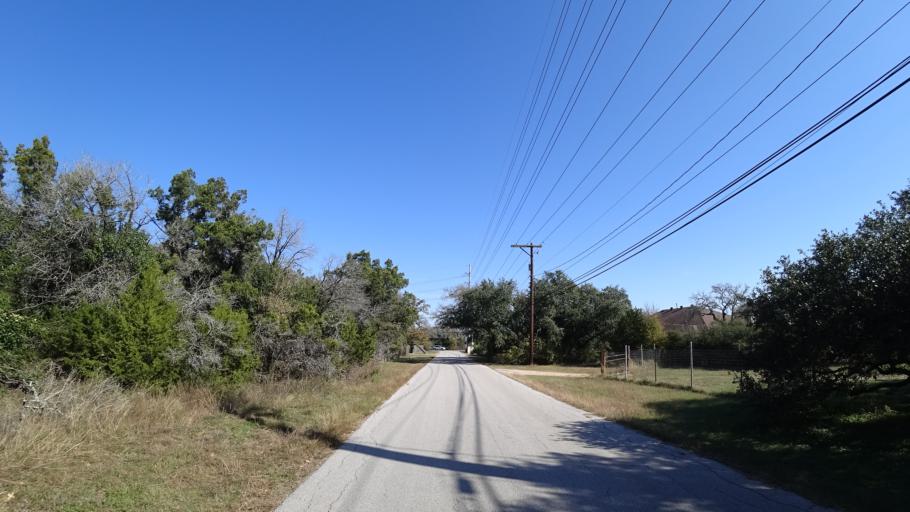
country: US
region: Texas
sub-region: Travis County
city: Barton Creek
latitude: 30.2320
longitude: -97.8578
